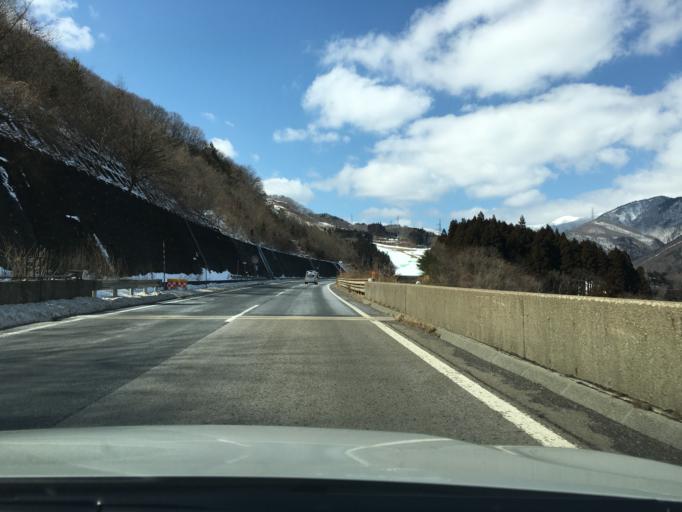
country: JP
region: Yamagata
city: Yamagata-shi
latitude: 38.2154
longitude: 140.5253
